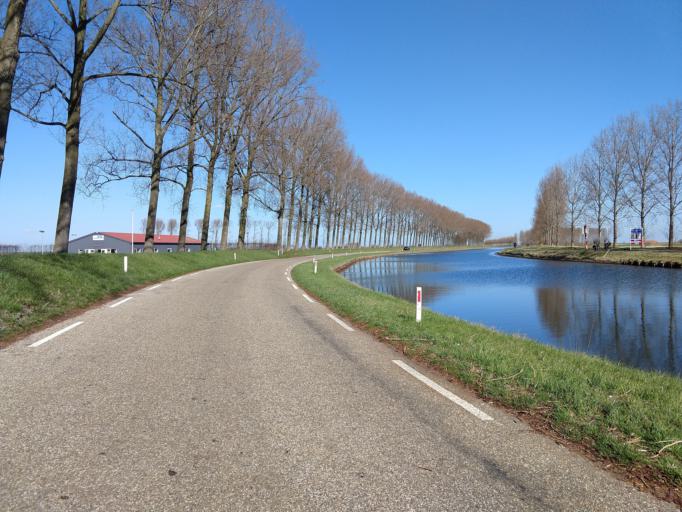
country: NL
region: Zeeland
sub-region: Gemeente Goes
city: Goes
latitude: 51.5324
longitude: 3.9013
